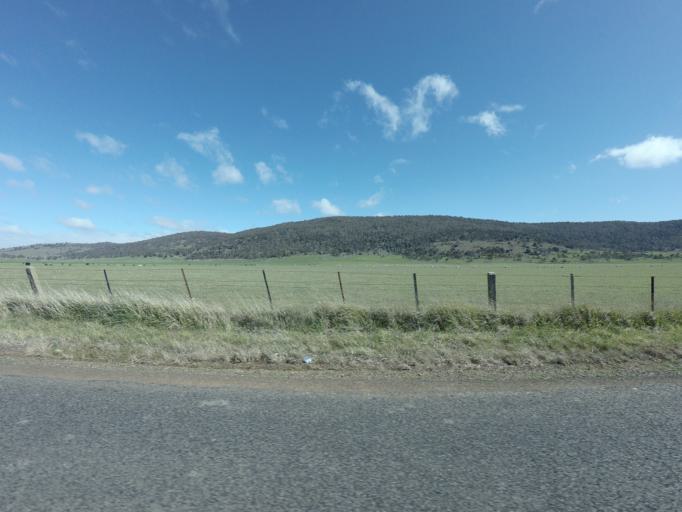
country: AU
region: Tasmania
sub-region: Northern Midlands
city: Evandale
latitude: -41.9730
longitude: 147.4442
